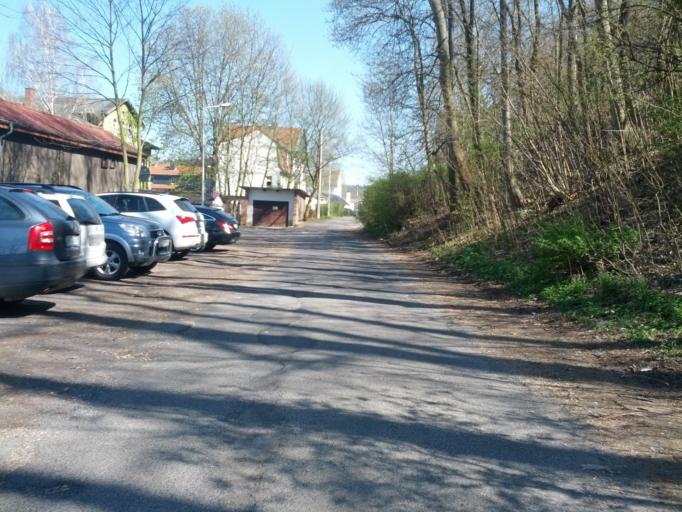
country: DE
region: Thuringia
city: Eisenach
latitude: 50.9756
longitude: 10.3318
